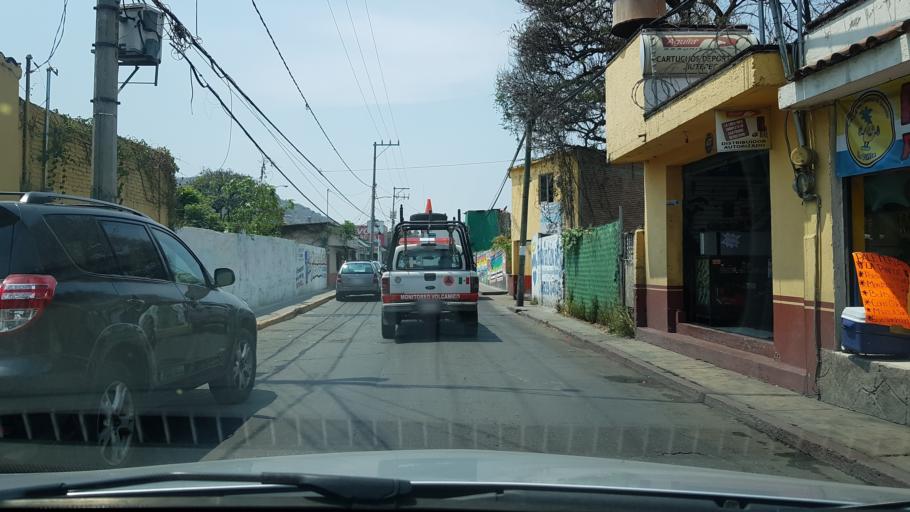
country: MX
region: Morelos
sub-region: Jiutepec
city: Jiutepec
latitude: 18.8812
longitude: -99.1784
